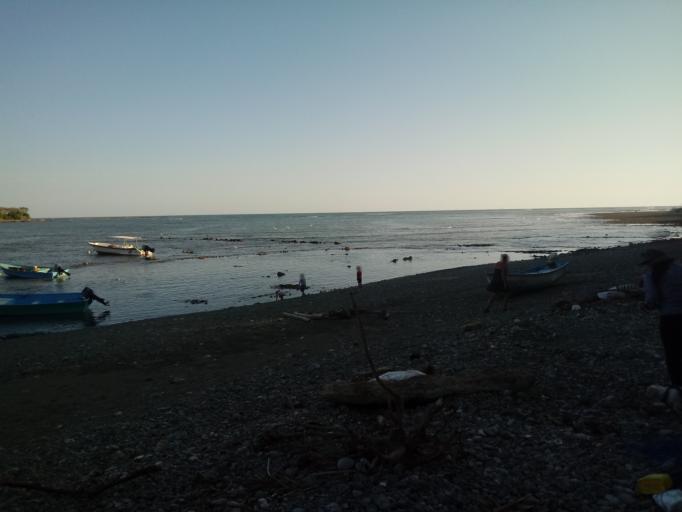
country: CR
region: Puntarenas
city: Paquera
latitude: 9.5986
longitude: -85.0854
